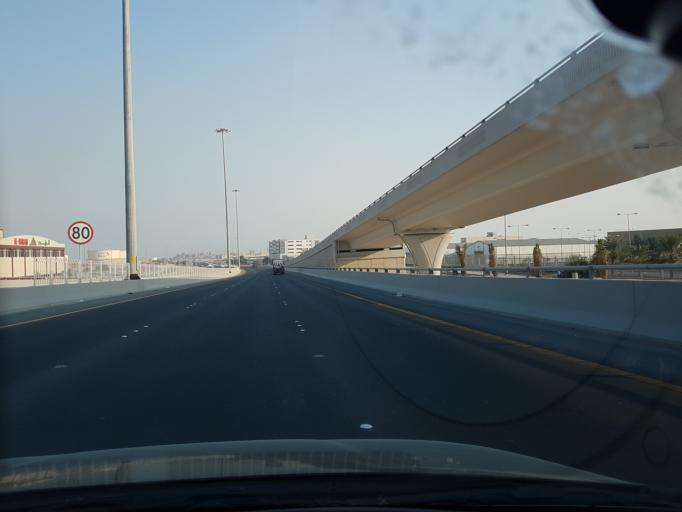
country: BH
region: Northern
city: Ar Rifa'
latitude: 26.1219
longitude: 50.5918
